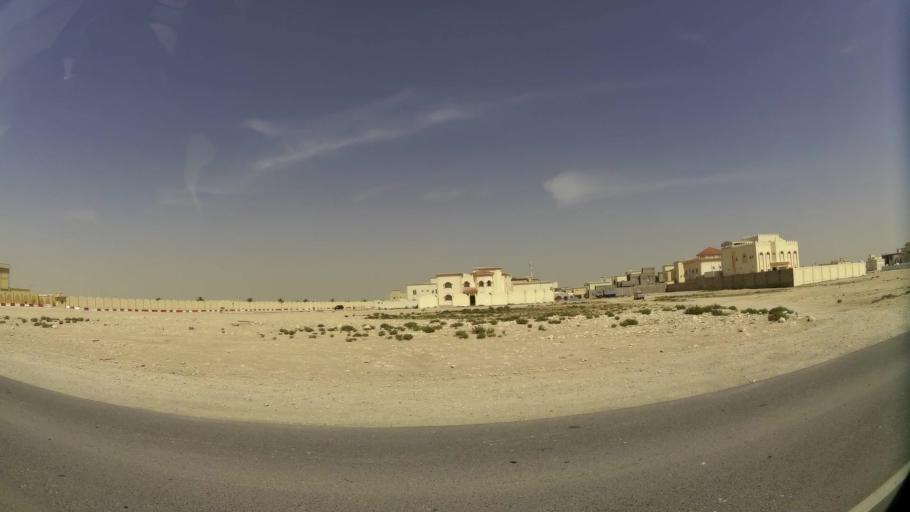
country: QA
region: Baladiyat ar Rayyan
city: Ar Rayyan
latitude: 25.2513
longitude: 51.3863
